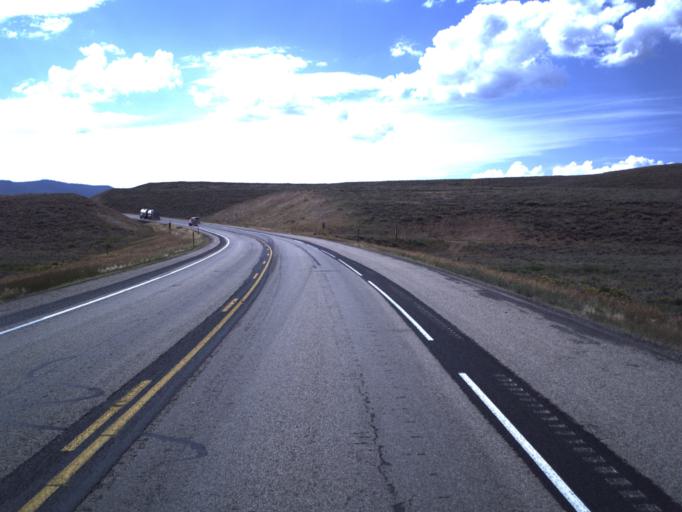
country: US
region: Utah
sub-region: Wasatch County
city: Heber
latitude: 40.2300
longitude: -111.1206
